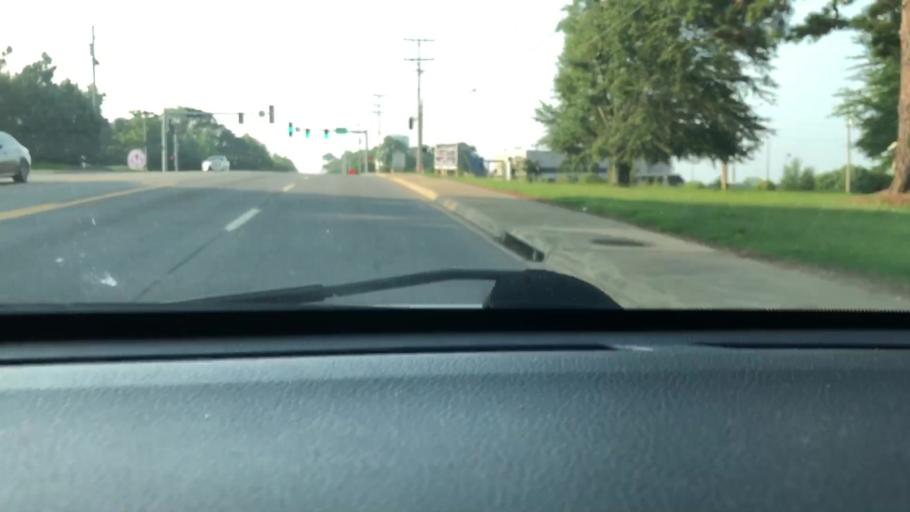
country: US
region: Arkansas
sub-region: Saline County
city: Bryant
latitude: 34.6037
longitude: -92.4910
